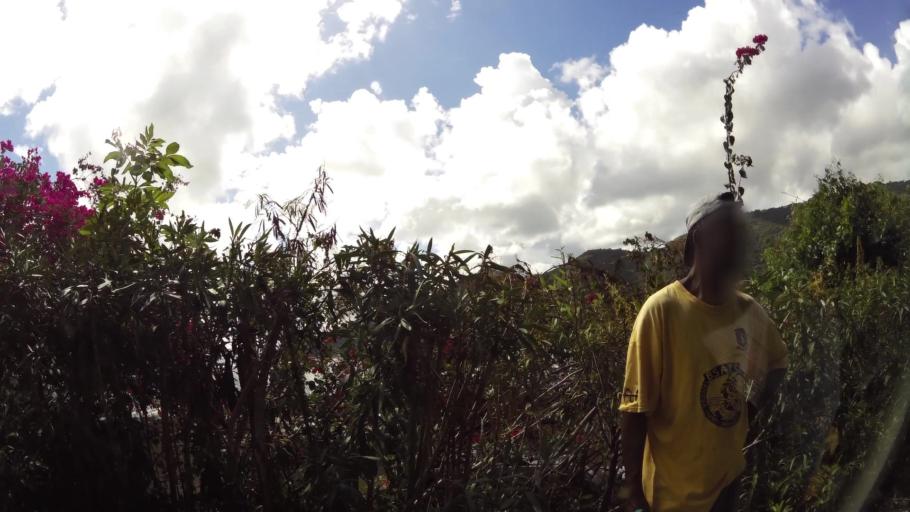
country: VG
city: Road Town
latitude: 18.4289
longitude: -64.6191
